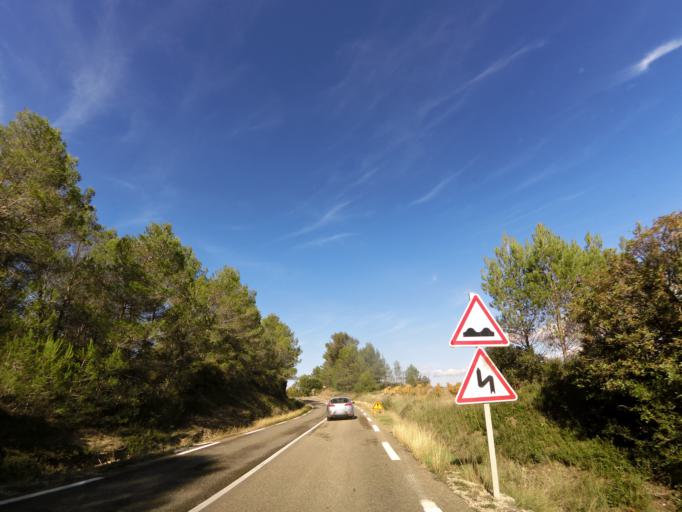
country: FR
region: Languedoc-Roussillon
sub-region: Departement du Gard
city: Ledignan
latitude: 43.9460
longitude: 4.1009
